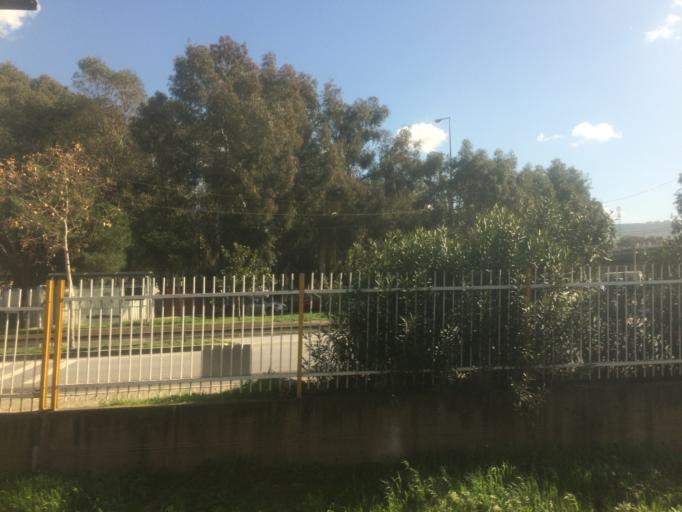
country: TR
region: Izmir
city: Buca
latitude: 38.4395
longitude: 27.1733
